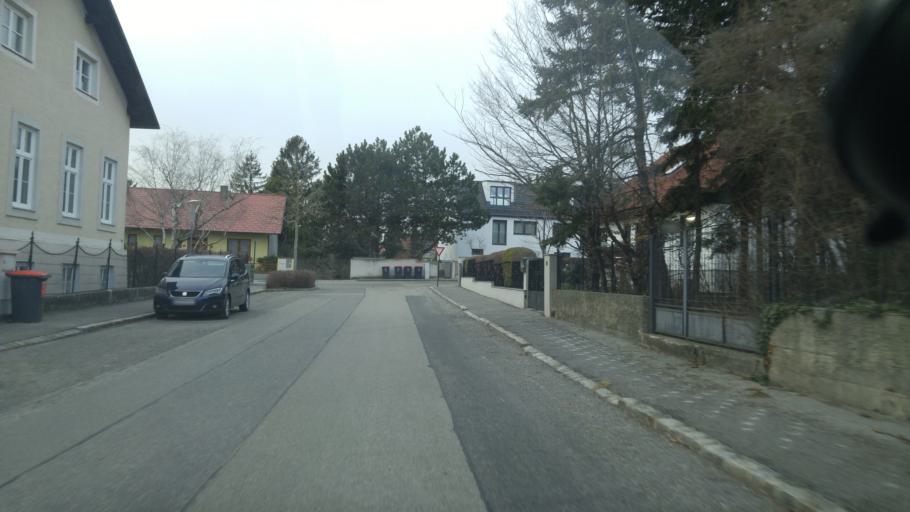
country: AT
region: Lower Austria
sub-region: Politischer Bezirk Baden
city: Bad Voslau
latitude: 47.9632
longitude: 16.2065
